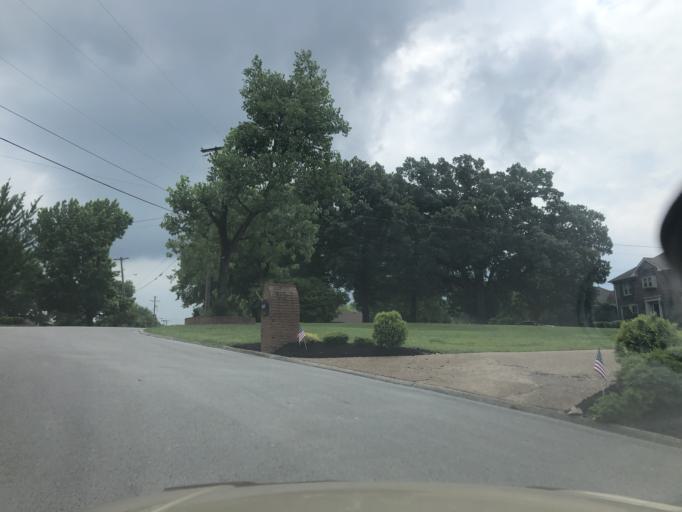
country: US
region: Tennessee
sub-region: Davidson County
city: Lakewood
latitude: 36.2420
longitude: -86.6116
